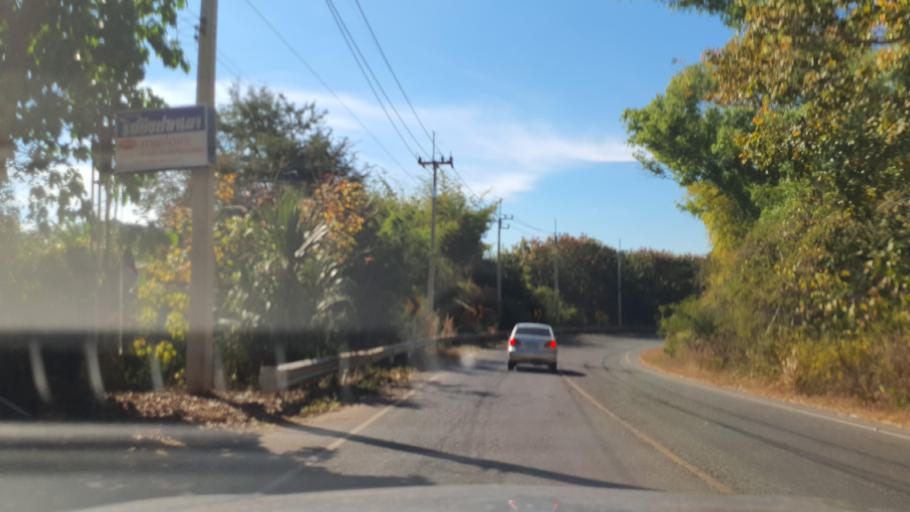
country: TH
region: Kalasin
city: Khao Wong
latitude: 16.7617
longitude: 104.1511
